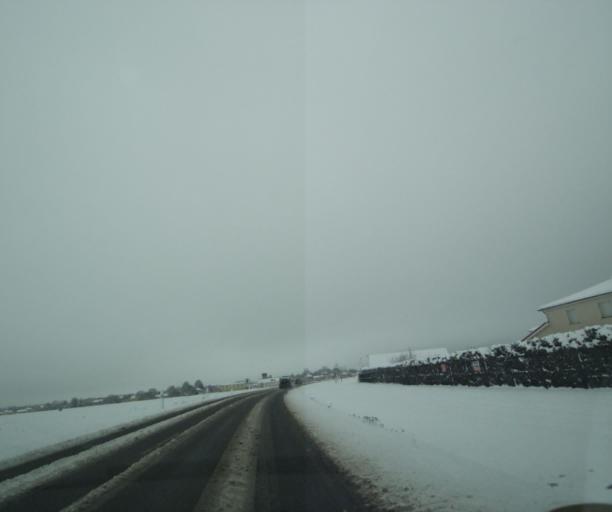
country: FR
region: Champagne-Ardenne
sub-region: Departement de la Haute-Marne
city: Saint-Dizier
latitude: 48.5778
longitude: 4.9074
